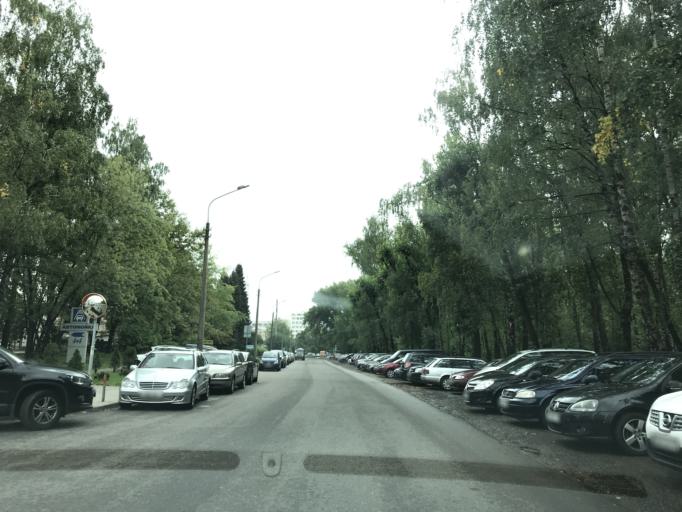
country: BY
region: Minsk
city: Minsk
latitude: 53.9463
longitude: 27.6158
